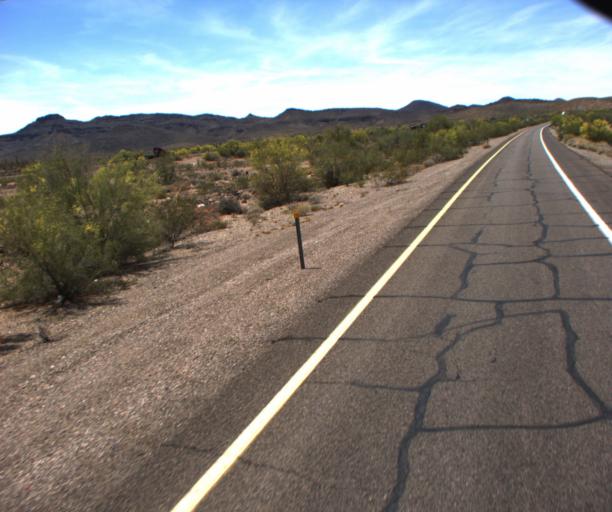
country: US
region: Arizona
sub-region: La Paz County
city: Quartzsite
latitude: 33.6637
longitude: -114.0106
